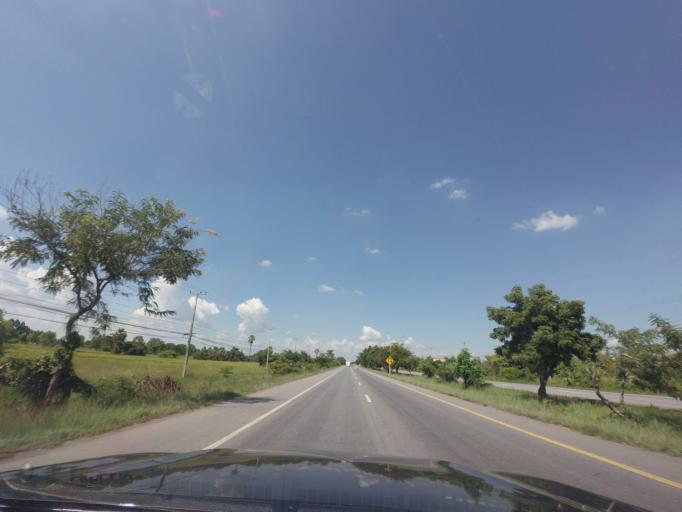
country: TH
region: Nakhon Ratchasima
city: Non Sung
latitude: 15.1561
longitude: 102.3286
